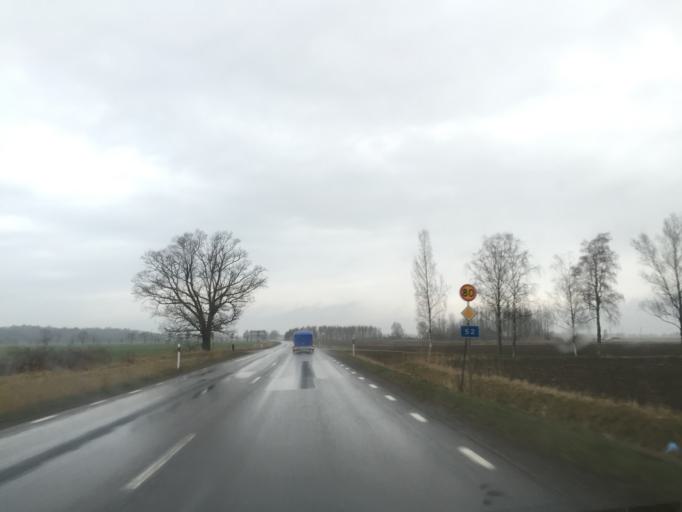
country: SE
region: OErebro
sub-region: Orebro Kommun
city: Odensbacken
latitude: 59.1467
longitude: 15.5749
